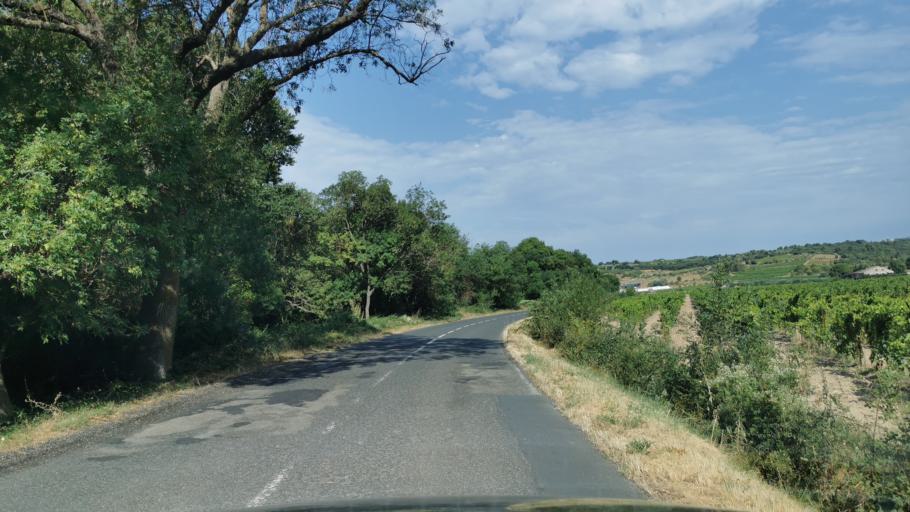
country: FR
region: Languedoc-Roussillon
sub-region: Departement de l'Aude
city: Bize-Minervois
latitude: 43.3433
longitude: 2.8668
